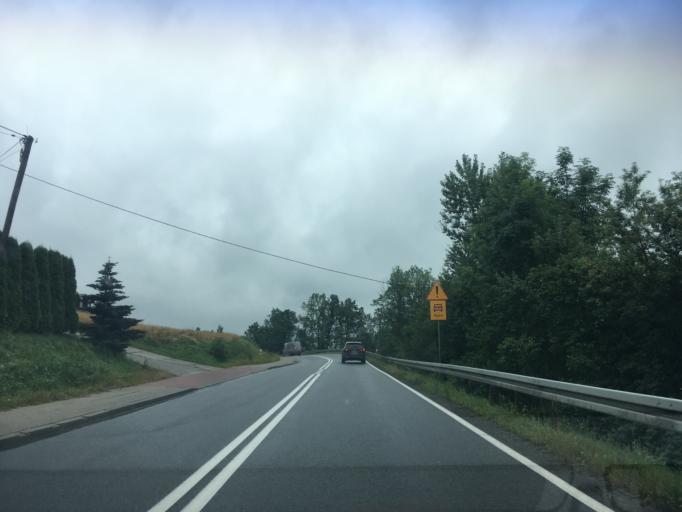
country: PL
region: Lesser Poland Voivodeship
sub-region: Powiat limanowski
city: Olszowka
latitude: 49.6382
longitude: 20.0271
